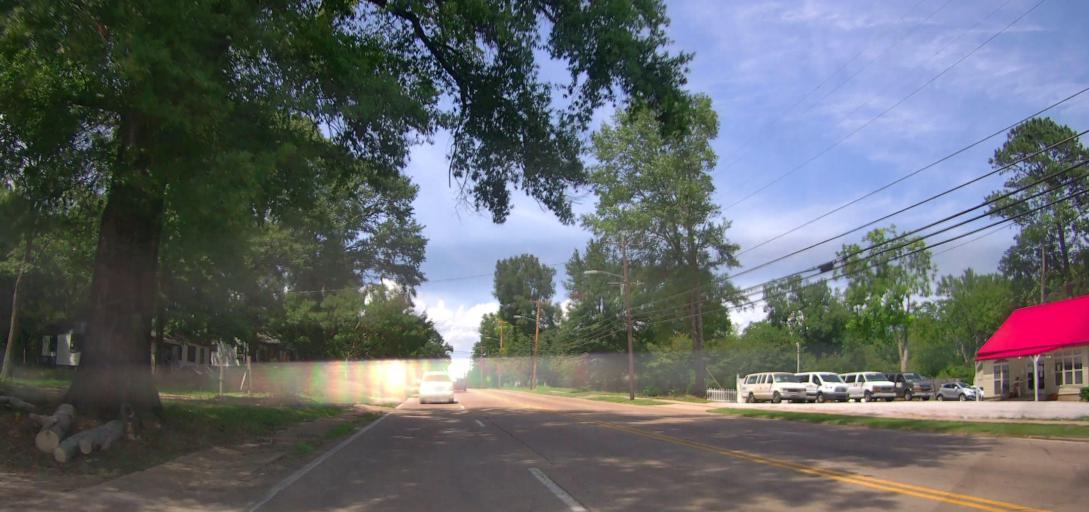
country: US
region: Mississippi
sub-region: Lee County
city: Verona
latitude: 34.1996
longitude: -88.7201
